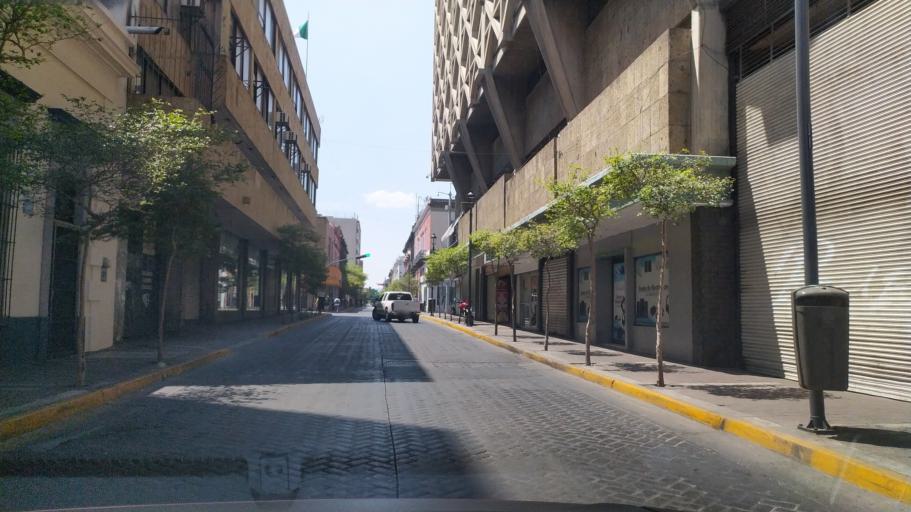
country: MX
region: Jalisco
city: Guadalajara
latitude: 20.6737
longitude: -103.3458
